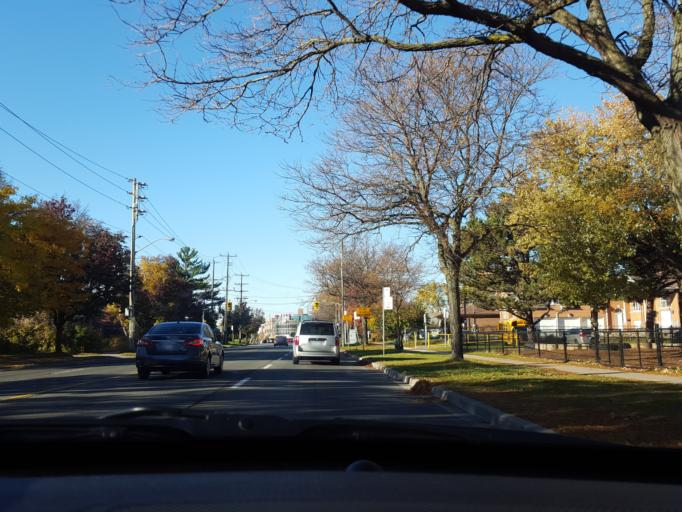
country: CA
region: Ontario
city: Scarborough
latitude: 43.7846
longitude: -79.2668
